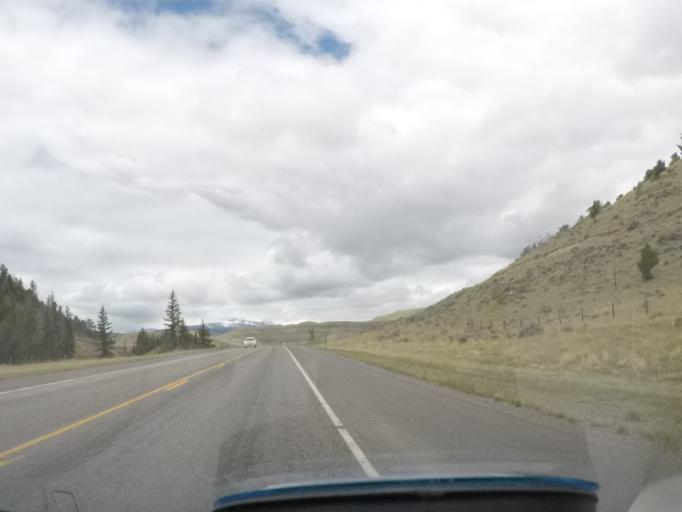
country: US
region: Wyoming
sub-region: Sublette County
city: Pinedale
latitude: 43.5805
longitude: -109.7630
